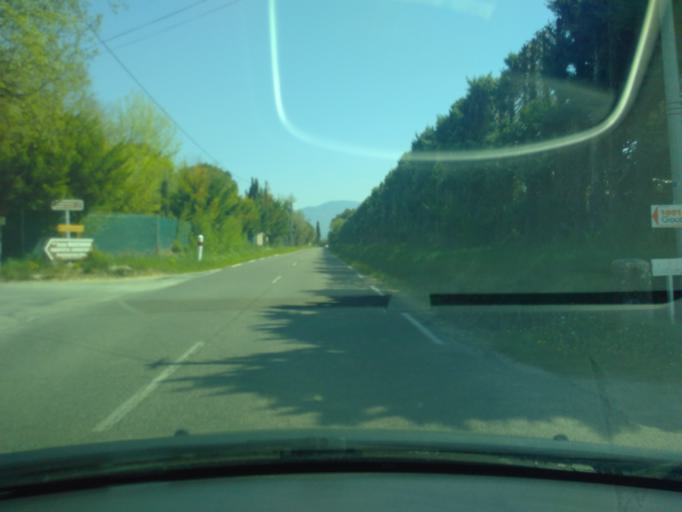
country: FR
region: Provence-Alpes-Cote d'Azur
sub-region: Departement du Vaucluse
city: Carpentras
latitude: 44.0752
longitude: 5.0777
